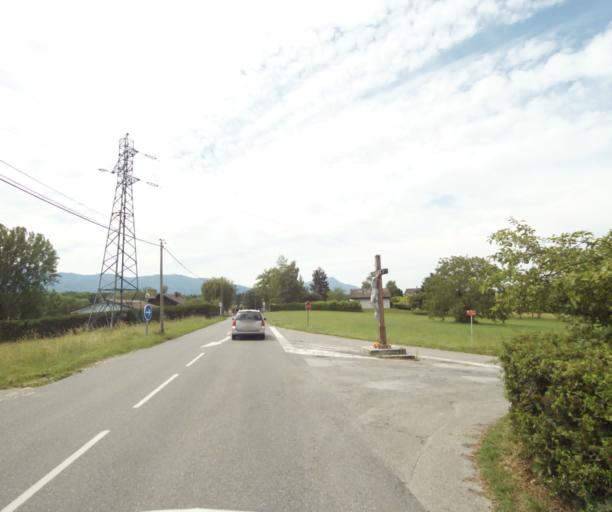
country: FR
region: Rhone-Alpes
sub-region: Departement de la Haute-Savoie
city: Margencel
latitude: 46.3351
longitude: 6.4323
